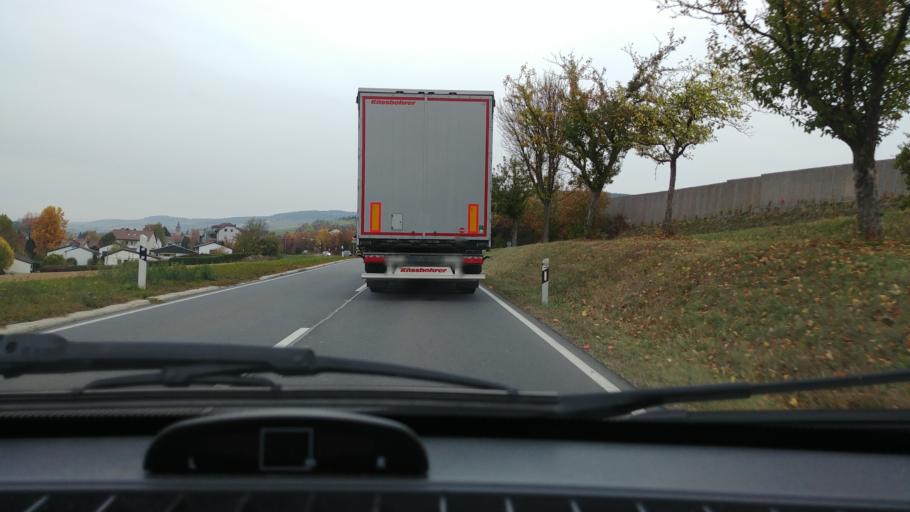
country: DE
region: Baden-Wuerttemberg
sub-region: Regierungsbezirk Stuttgart
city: Bad Mergentheim
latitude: 49.5069
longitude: 9.7532
